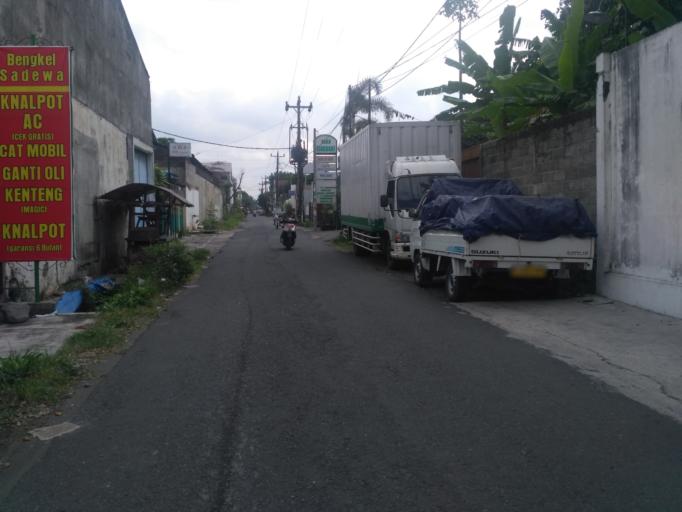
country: ID
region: Daerah Istimewa Yogyakarta
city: Melati
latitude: -7.7577
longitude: 110.3630
